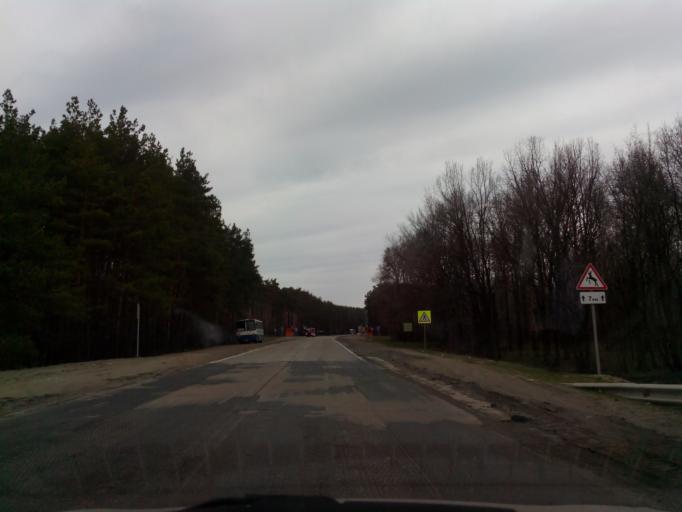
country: RU
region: Tambov
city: Znamenka
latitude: 52.5325
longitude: 41.3564
